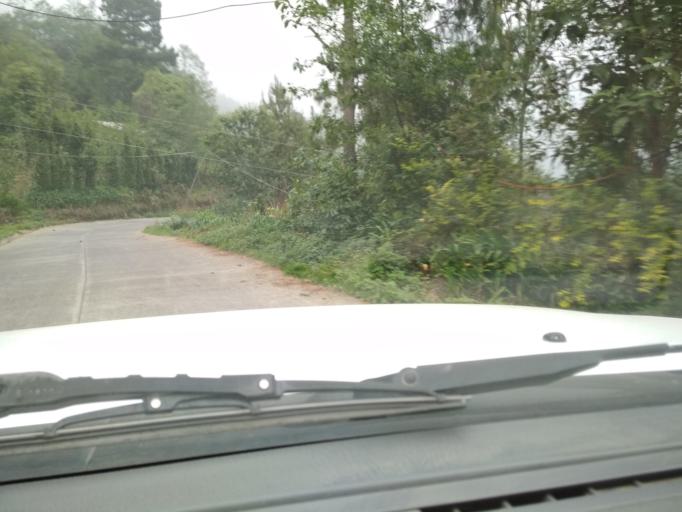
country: MX
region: Veracruz
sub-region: La Perla
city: Chilapa
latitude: 18.9730
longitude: -97.1636
